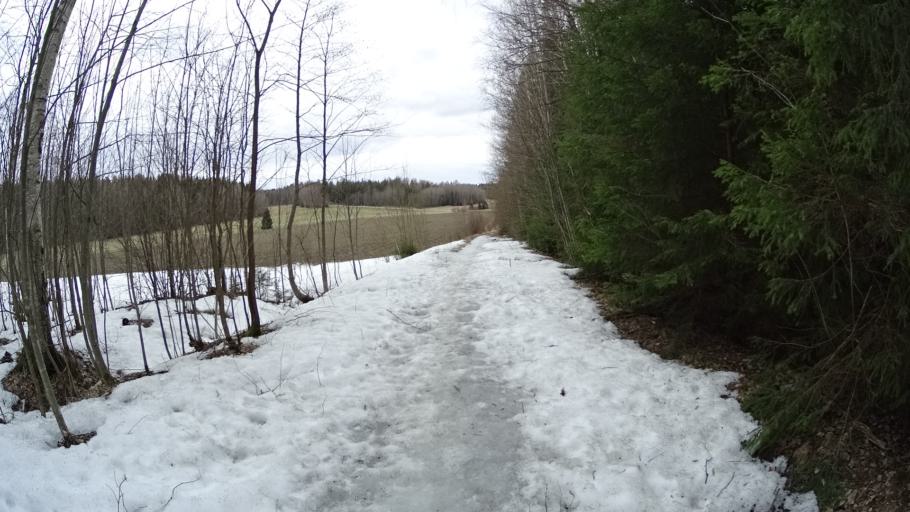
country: FI
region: Uusimaa
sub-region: Helsinki
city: Kilo
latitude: 60.2857
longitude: 24.8040
